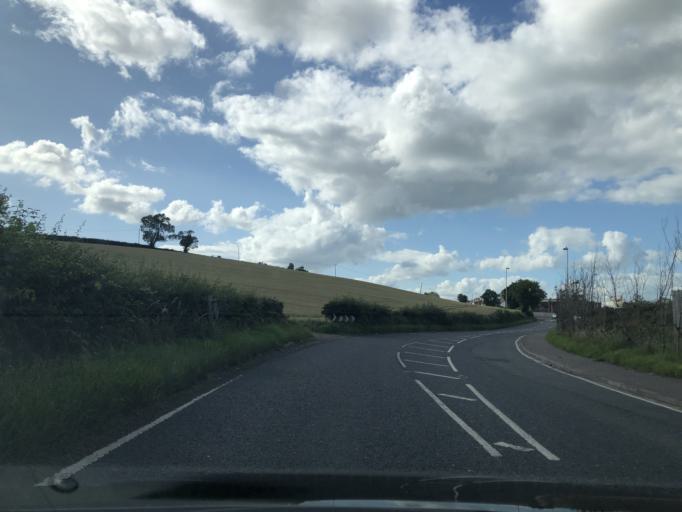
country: GB
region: Northern Ireland
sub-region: Castlereagh District
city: Dundonald
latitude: 54.5801
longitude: -5.7922
